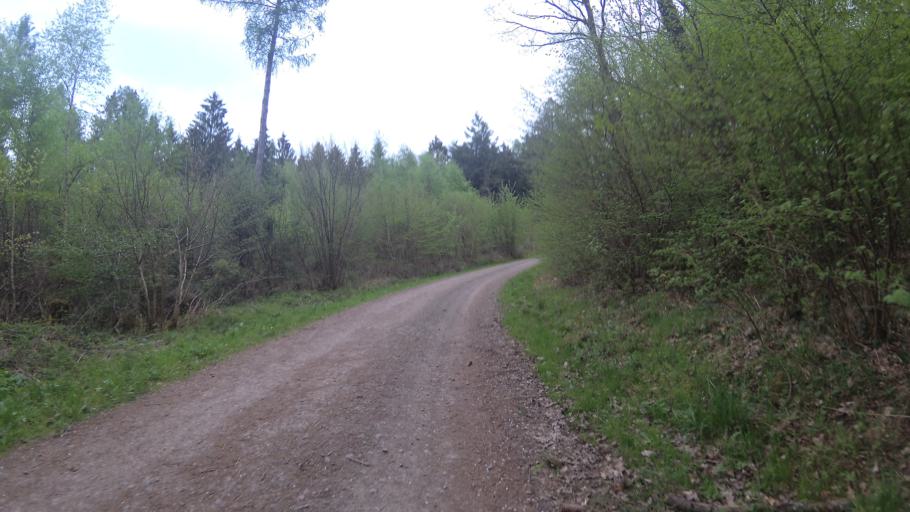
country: DE
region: Saarland
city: Mainzweiler
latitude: 49.4253
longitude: 7.1364
